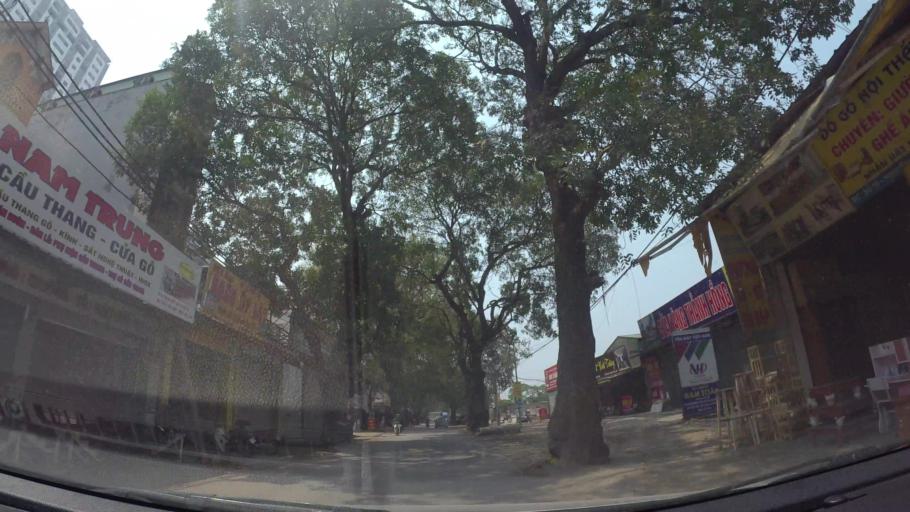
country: VN
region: Ha Noi
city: Ha Dong
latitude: 20.9862
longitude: 105.7677
